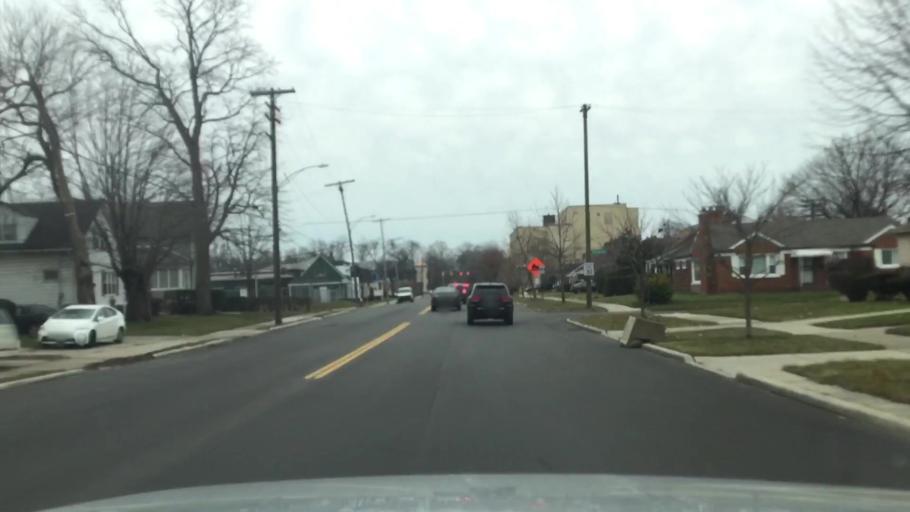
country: US
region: Michigan
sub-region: Wayne County
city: Grosse Pointe
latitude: 42.3972
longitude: -82.9241
